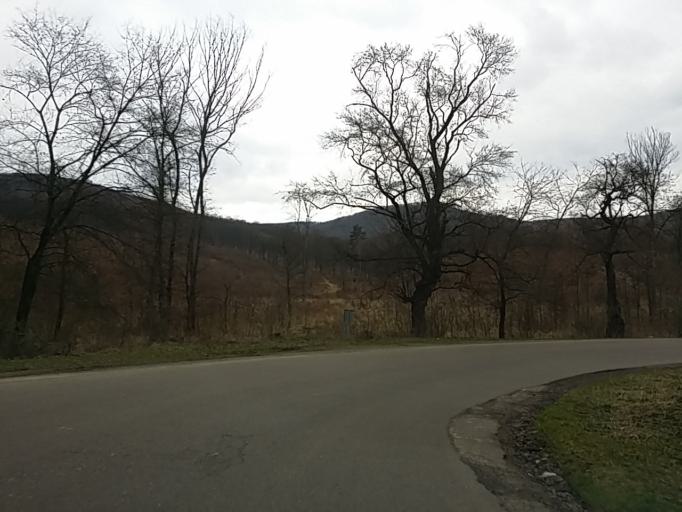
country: HU
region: Heves
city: Sirok
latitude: 47.8960
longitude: 20.1847
